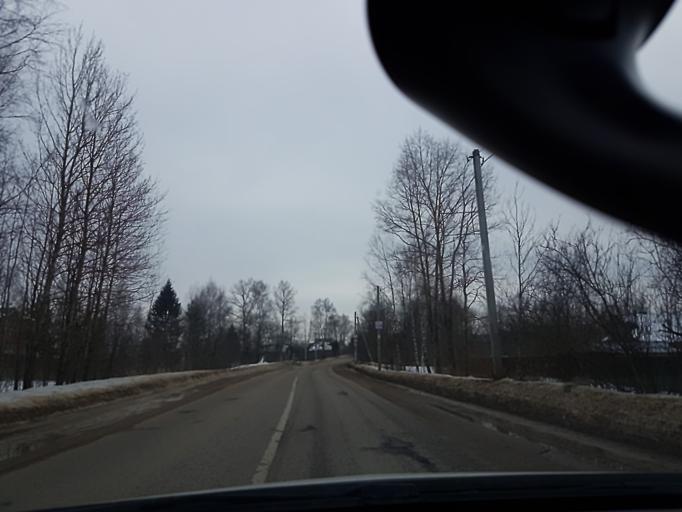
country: RU
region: Moskovskaya
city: Sychevo
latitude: 55.9923
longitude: 36.2238
